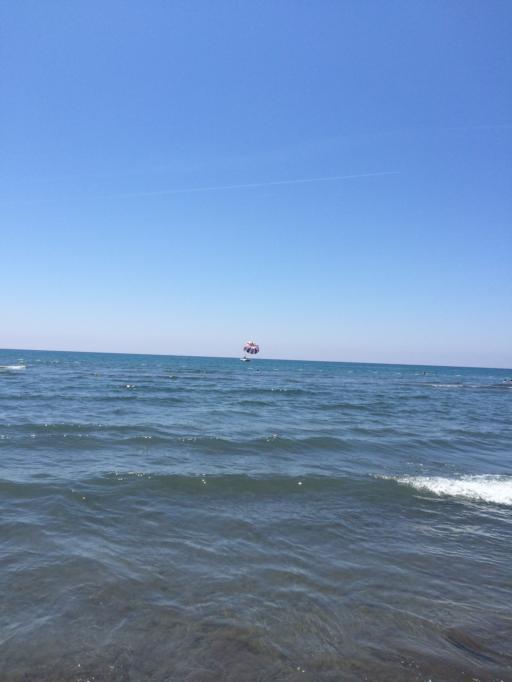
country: ME
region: Ulcinj
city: Ulcinj
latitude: 41.9087
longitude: 19.2424
